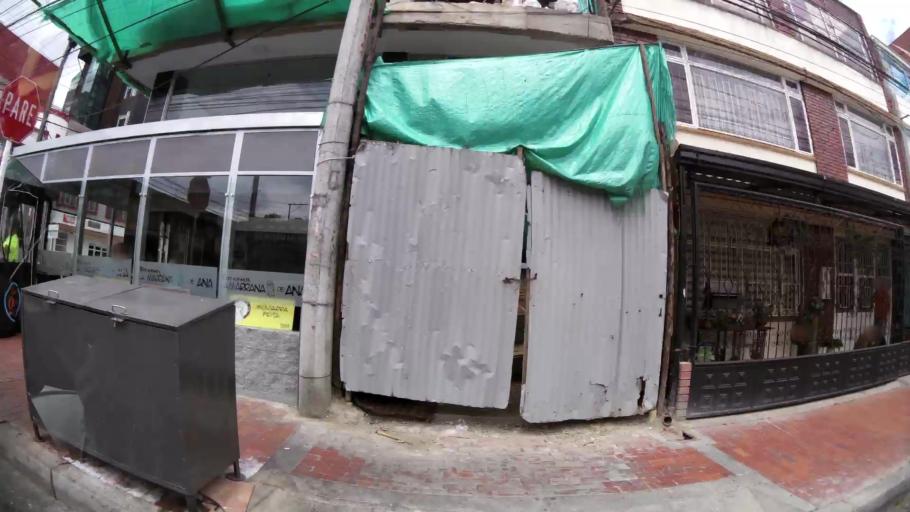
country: CO
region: Bogota D.C.
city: Bogota
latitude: 4.6331
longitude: -74.0950
